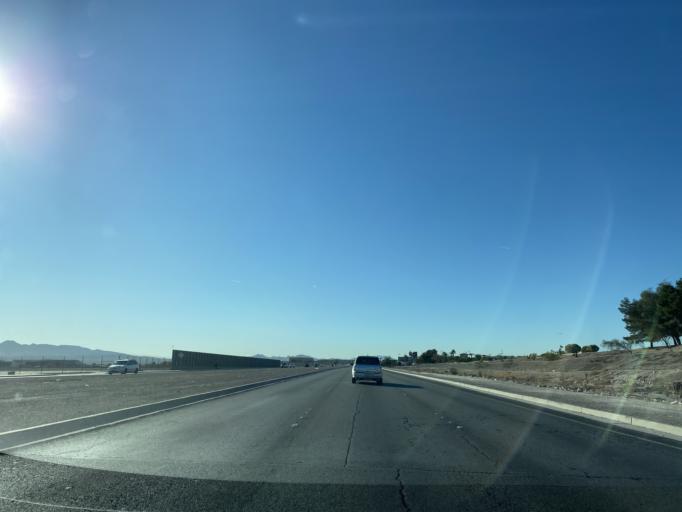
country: US
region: Nevada
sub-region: Clark County
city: Paradise
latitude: 36.0783
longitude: -115.1729
